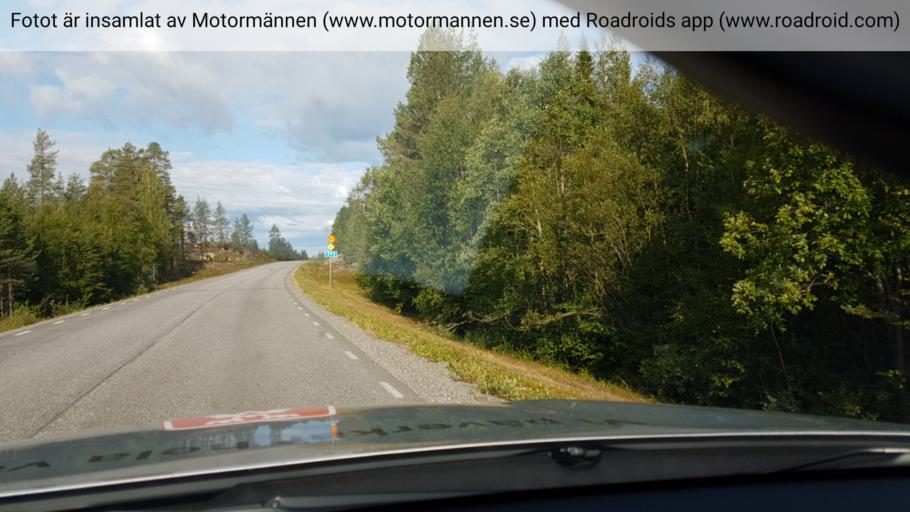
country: SE
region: Vaesterbotten
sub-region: Skelleftea Kommun
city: Storvik
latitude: 65.3304
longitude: 20.5963
